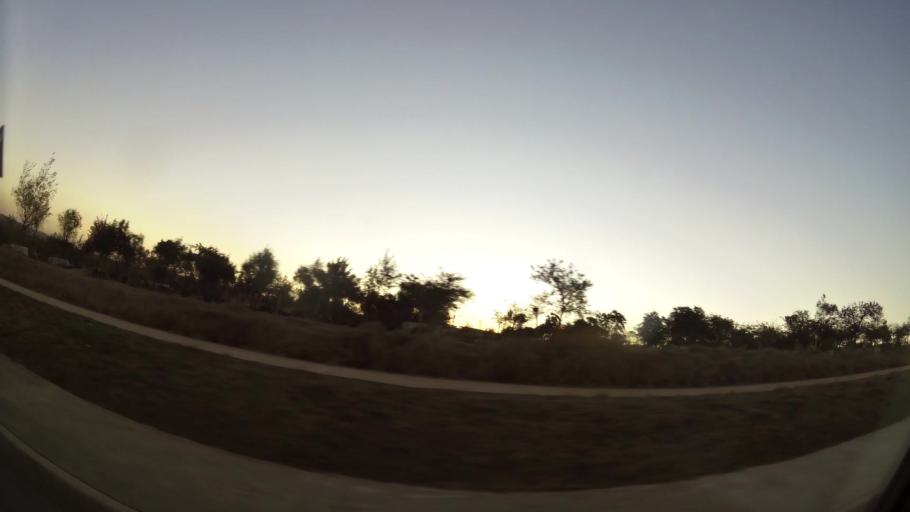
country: ZA
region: Gauteng
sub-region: City of Johannesburg Metropolitan Municipality
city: Diepsloot
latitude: -25.9758
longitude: 28.0198
